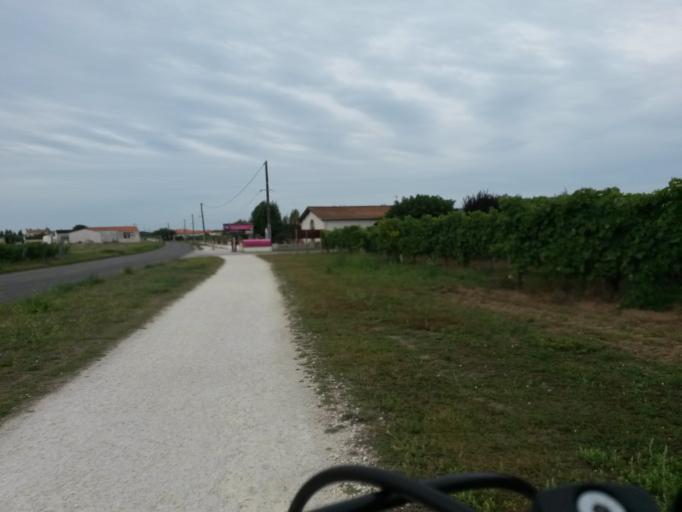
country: FR
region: Poitou-Charentes
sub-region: Departement de la Charente-Maritime
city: Dolus-d'Oleron
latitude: 45.9330
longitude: -1.3263
